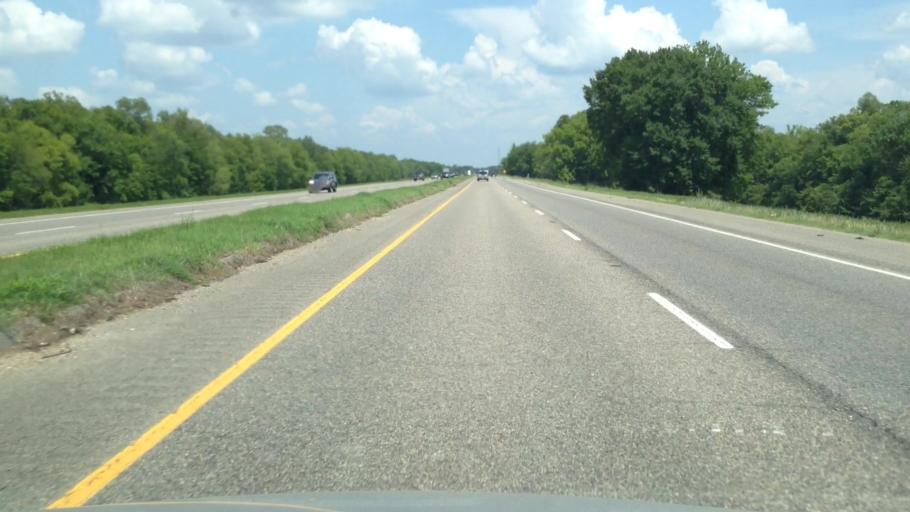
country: US
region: Louisiana
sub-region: Saint Landry Parish
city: Krotz Springs
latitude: 30.5441
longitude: -91.8024
